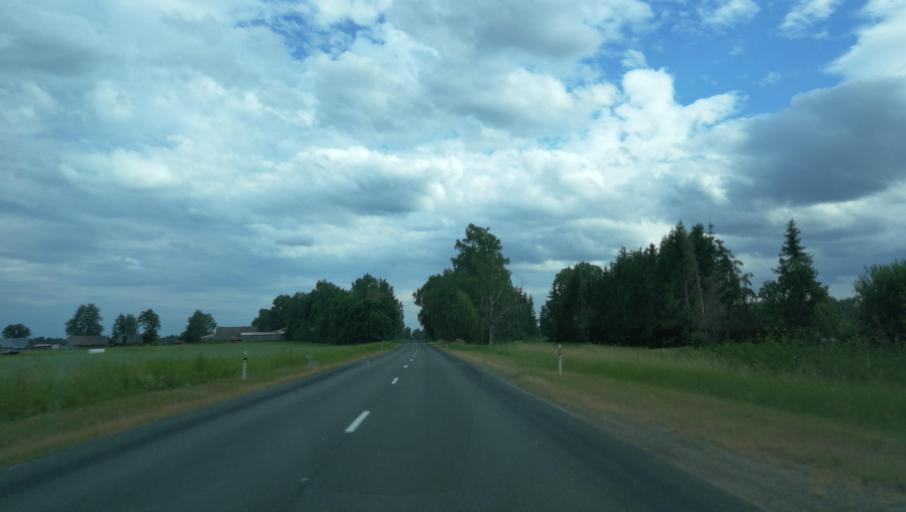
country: LV
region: Rujienas
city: Rujiena
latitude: 57.8523
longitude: 25.3788
